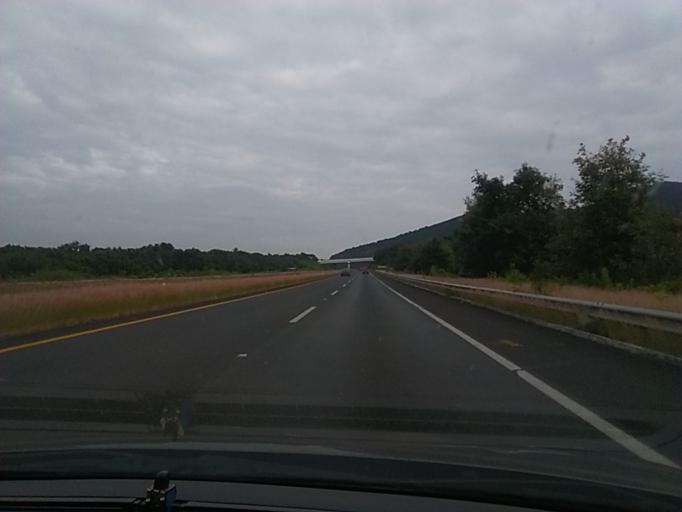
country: MX
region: Michoacan
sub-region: Puruandiro
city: San Lorenzo
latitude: 19.9640
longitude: -101.6959
